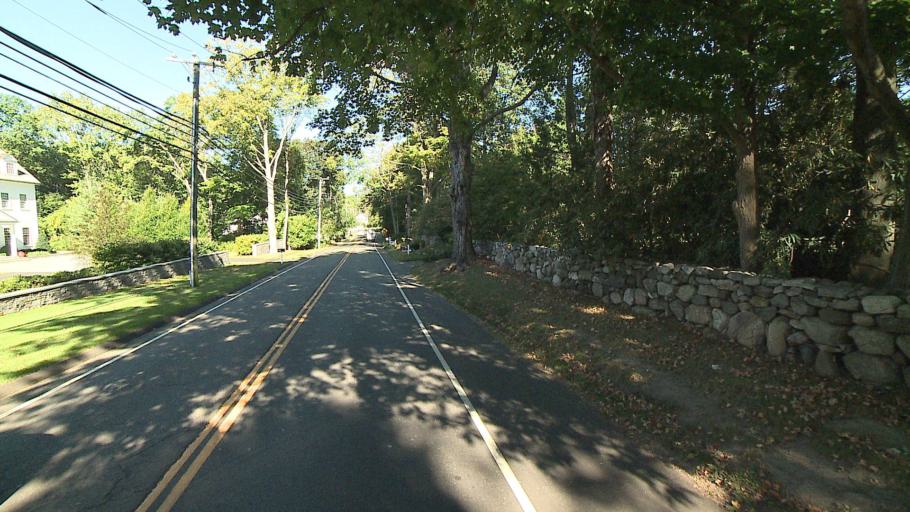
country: US
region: Connecticut
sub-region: Fairfield County
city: New Canaan
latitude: 41.1579
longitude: -73.5013
